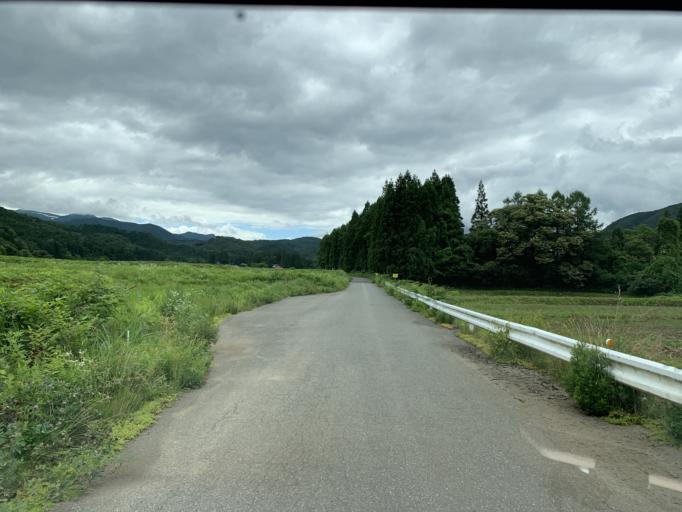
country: JP
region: Iwate
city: Ichinoseki
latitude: 38.9728
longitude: 140.9285
